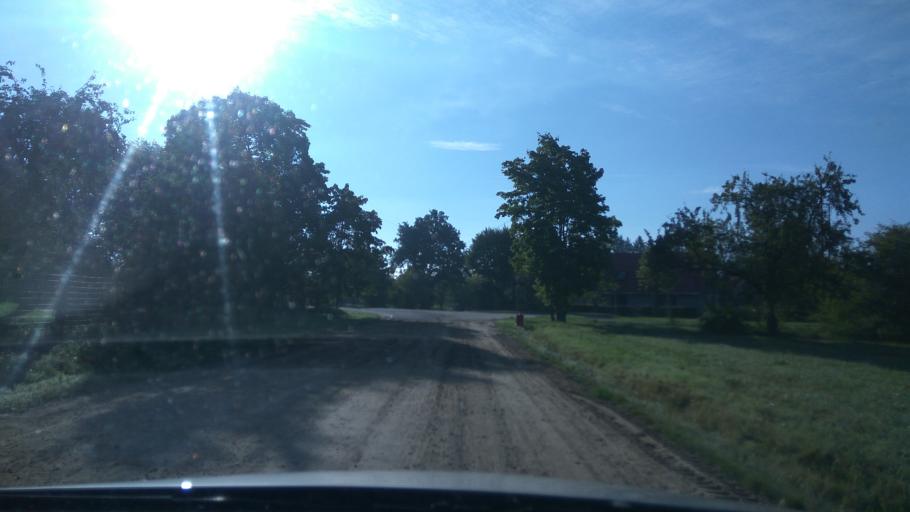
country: LV
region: Kuldigas Rajons
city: Kuldiga
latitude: 56.9724
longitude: 21.9952
